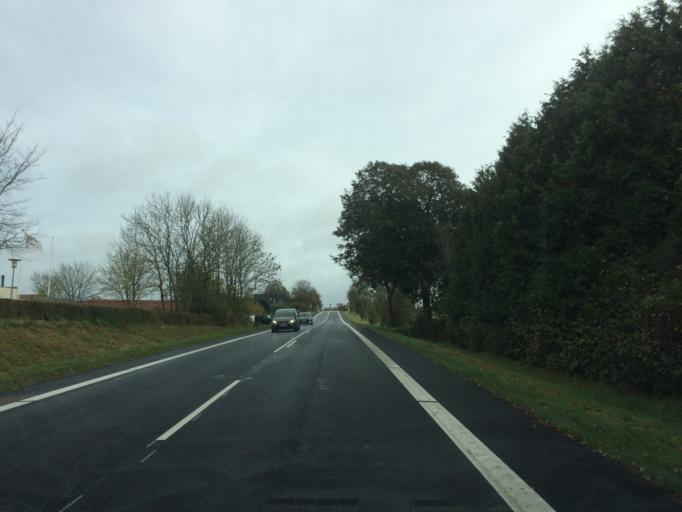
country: DK
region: South Denmark
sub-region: Fredericia Kommune
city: Taulov
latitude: 55.5326
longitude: 9.6140
